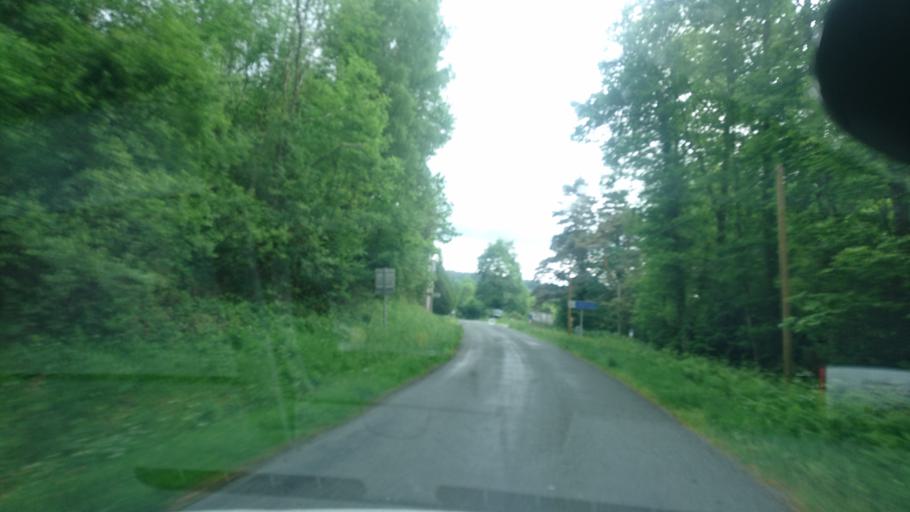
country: FR
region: Limousin
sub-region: Departement de la Haute-Vienne
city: Peyrat-le-Chateau
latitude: 45.8123
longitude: 1.8224
